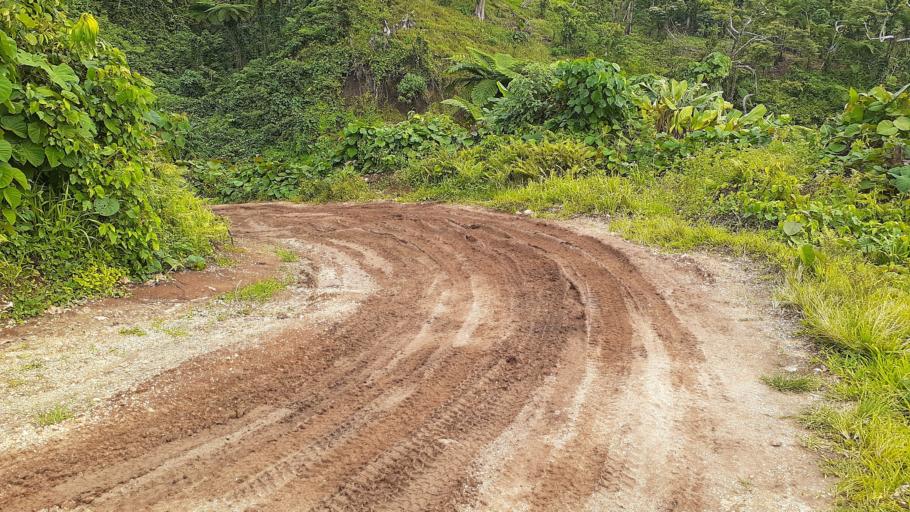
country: VU
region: Penama
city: Saratamata
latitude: -15.9612
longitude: 168.2101
